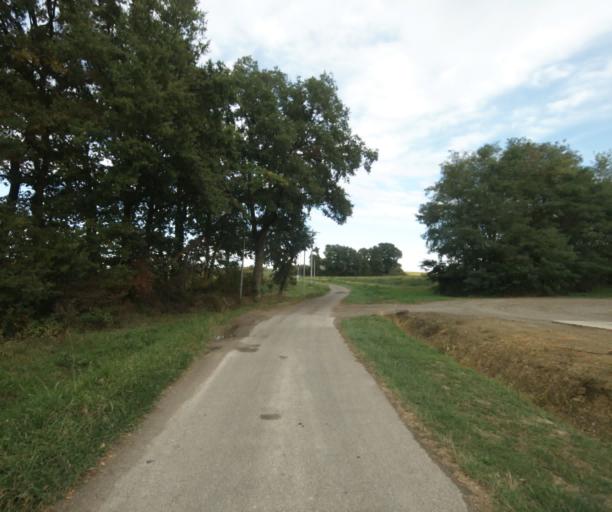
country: FR
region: Midi-Pyrenees
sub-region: Departement du Gers
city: Le Houga
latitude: 43.8549
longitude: -0.1305
